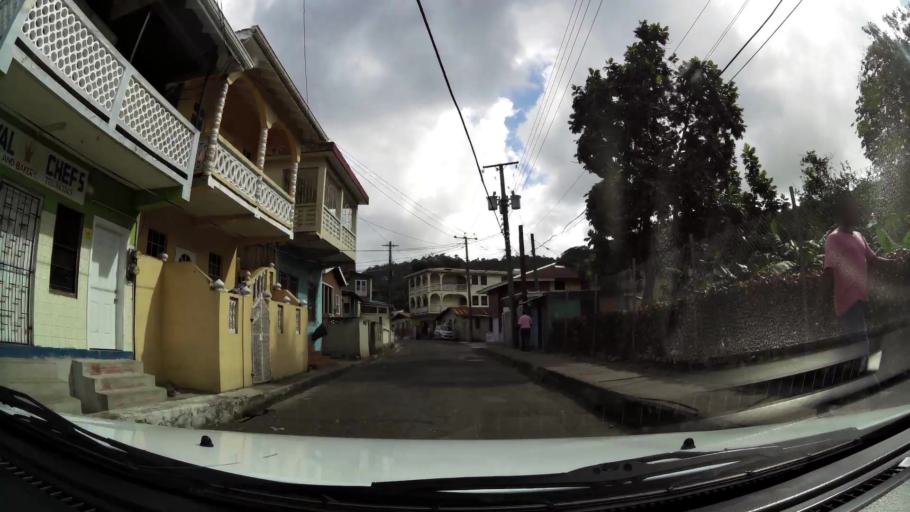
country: LC
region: Castries Quarter
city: Castries
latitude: 14.0049
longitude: -60.9873
